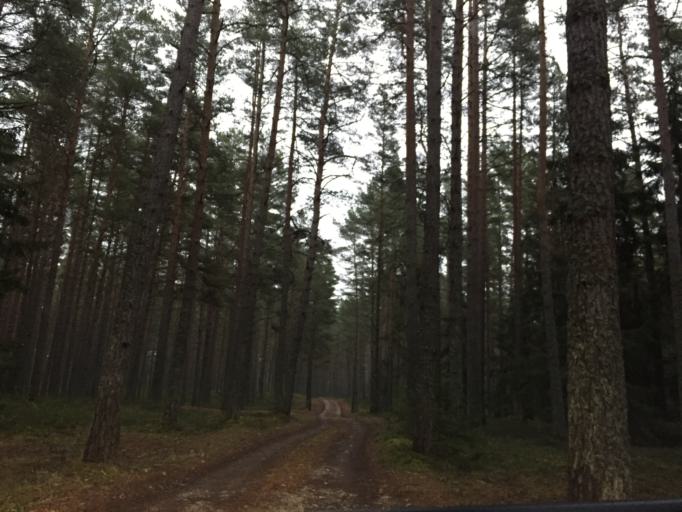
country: EE
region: Saare
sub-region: Kuressaare linn
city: Kuressaare
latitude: 58.5919
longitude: 22.5080
